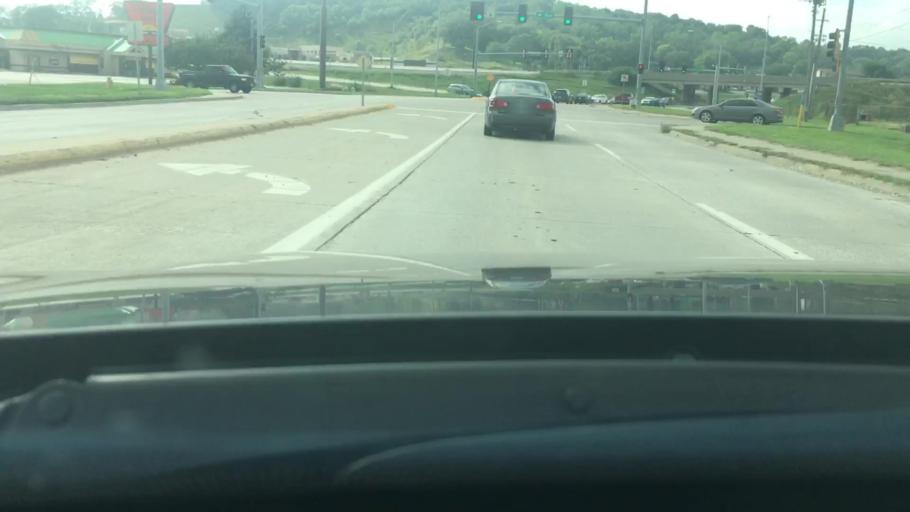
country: US
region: Iowa
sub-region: Pottawattamie County
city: Council Bluffs
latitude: 41.2415
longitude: -95.8203
